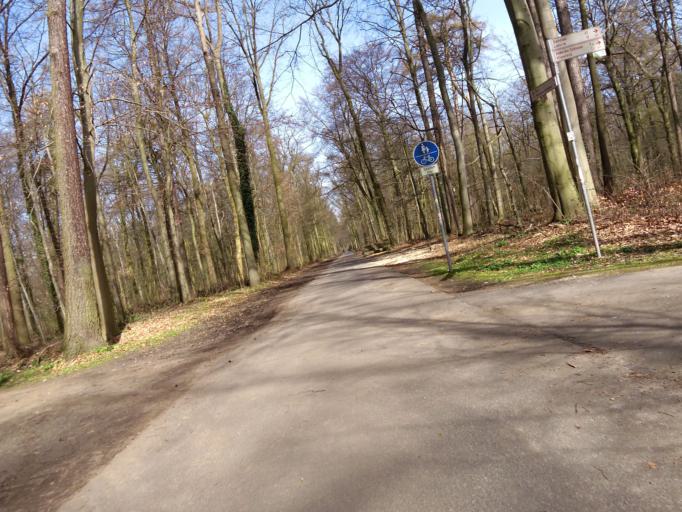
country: DE
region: Lower Saxony
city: Laatzen
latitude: 52.3615
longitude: 9.7865
